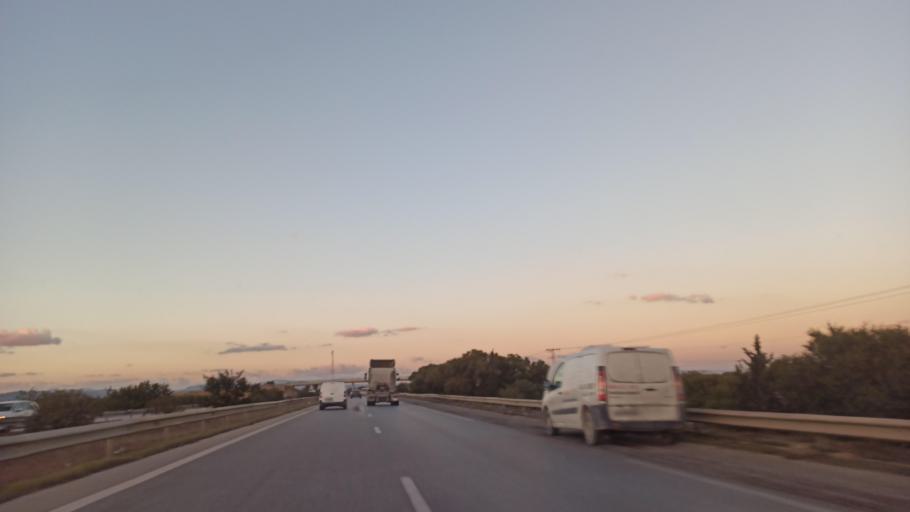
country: TN
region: Nabul
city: Al Hammamat
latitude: 36.2600
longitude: 10.4286
